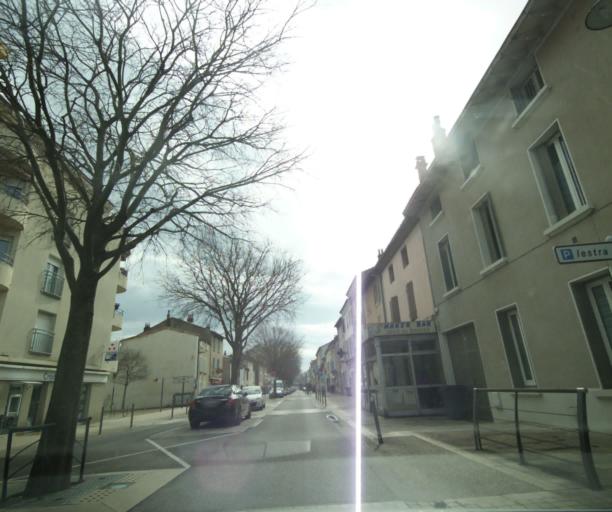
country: FR
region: Rhone-Alpes
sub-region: Departement de la Drome
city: Valence
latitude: 44.9445
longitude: 4.8940
